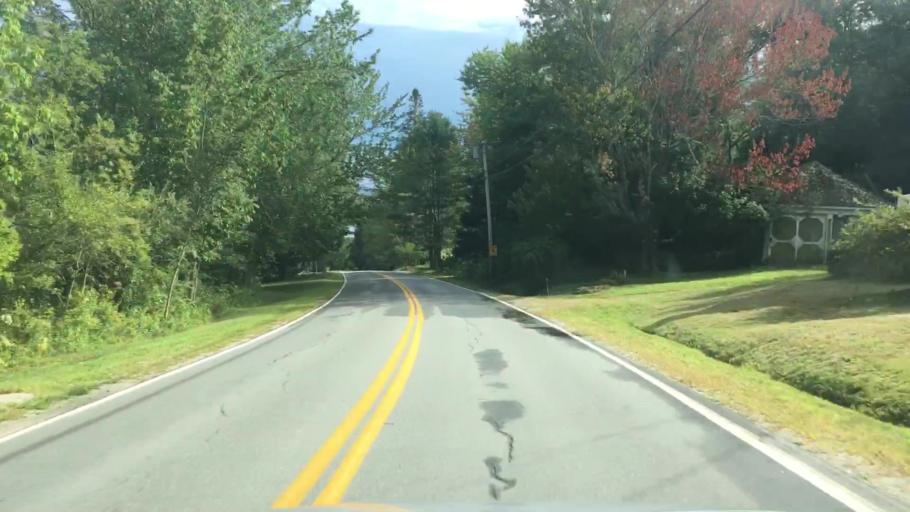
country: US
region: Maine
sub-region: Hancock County
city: Trenton
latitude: 44.4328
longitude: -68.3979
